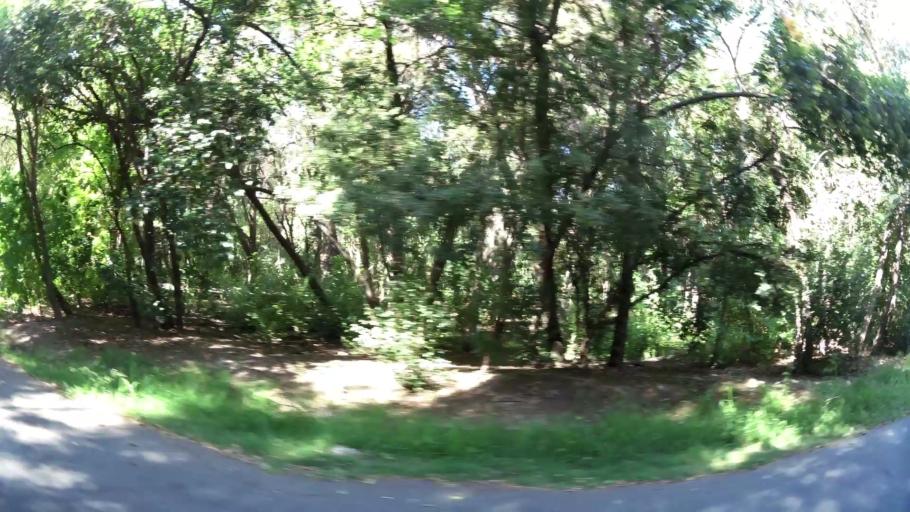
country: AR
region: Mendoza
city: Mendoza
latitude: -32.8860
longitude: -68.8697
